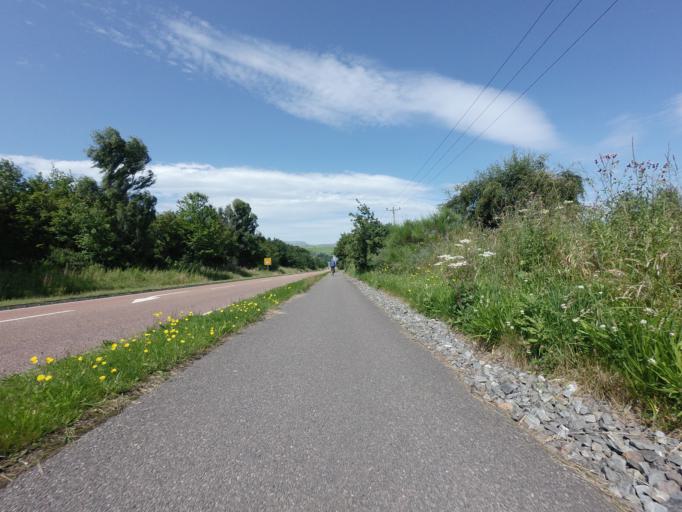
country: GB
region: Scotland
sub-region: Highland
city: Conon Bridge
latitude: 57.5685
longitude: -4.4257
